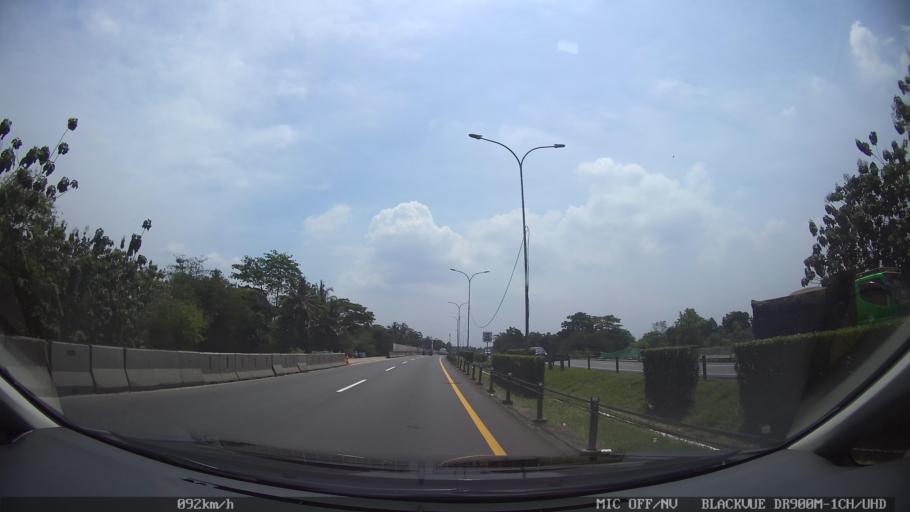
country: ID
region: Banten
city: Serang
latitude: -6.1385
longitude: 106.2233
